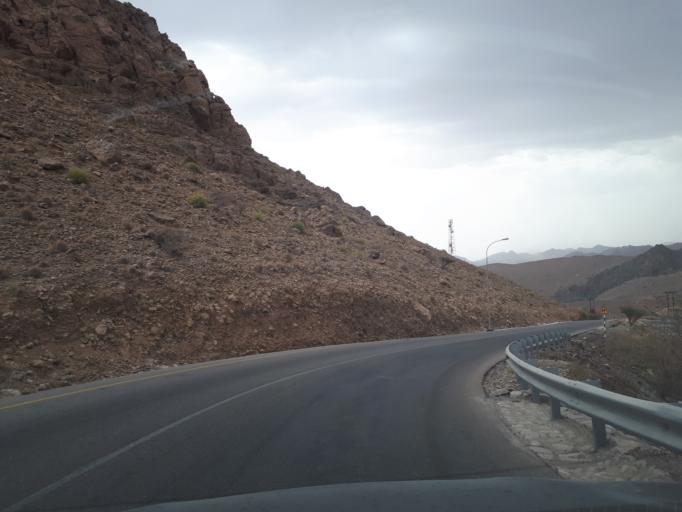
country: OM
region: Ash Sharqiyah
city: Badiyah
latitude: 22.5702
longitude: 59.0726
